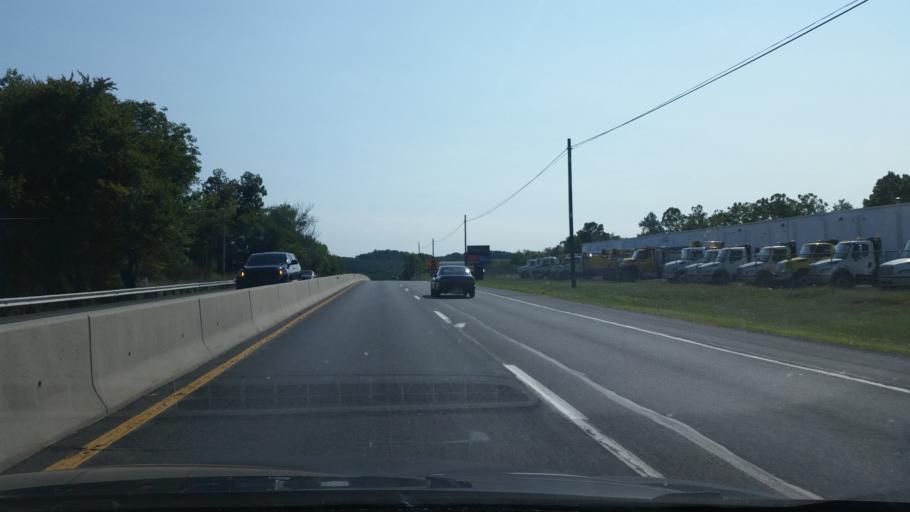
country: US
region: Pennsylvania
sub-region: Berks County
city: Leesport
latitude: 40.4703
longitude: -75.9687
